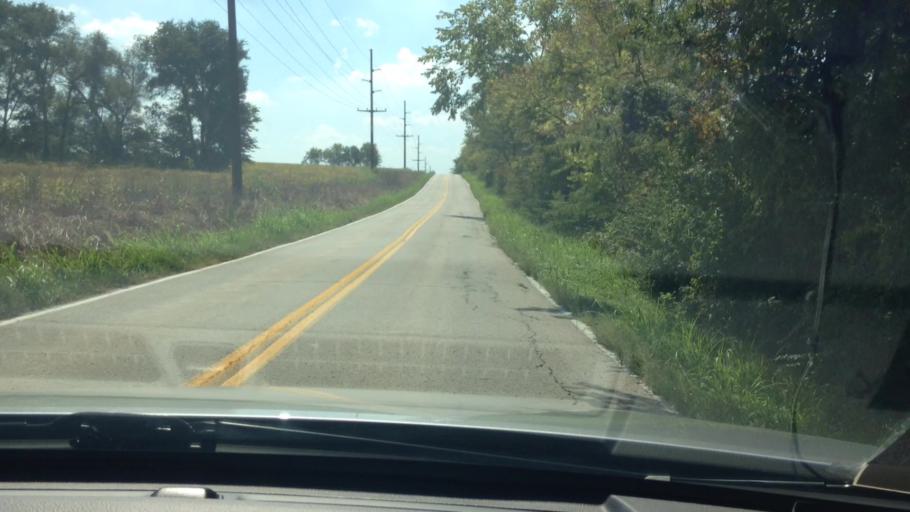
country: US
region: Missouri
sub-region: Platte County
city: Platte City
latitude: 39.3501
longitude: -94.7330
